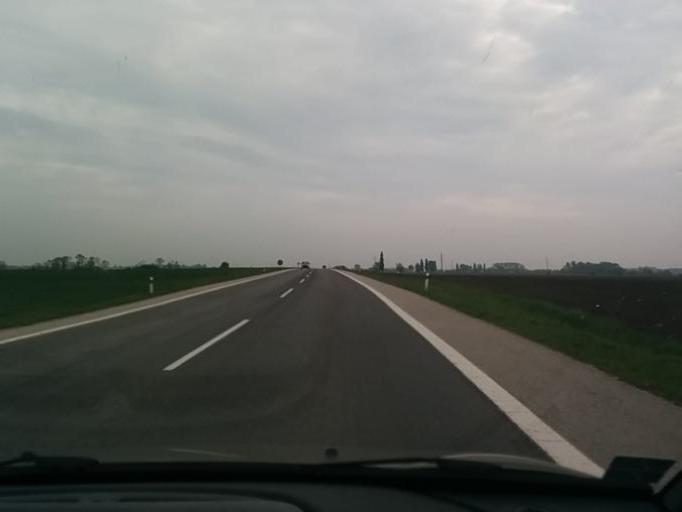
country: SK
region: Trnavsky
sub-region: Okres Galanta
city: Galanta
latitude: 48.2590
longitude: 17.7120
